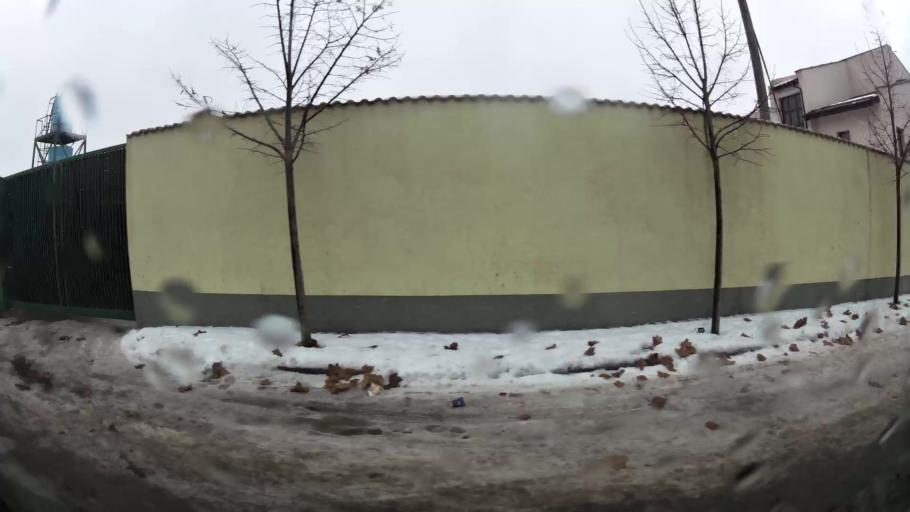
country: RO
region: Ilfov
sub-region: Comuna Bragadiru
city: Bragadiru
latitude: 44.3980
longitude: 26.0048
